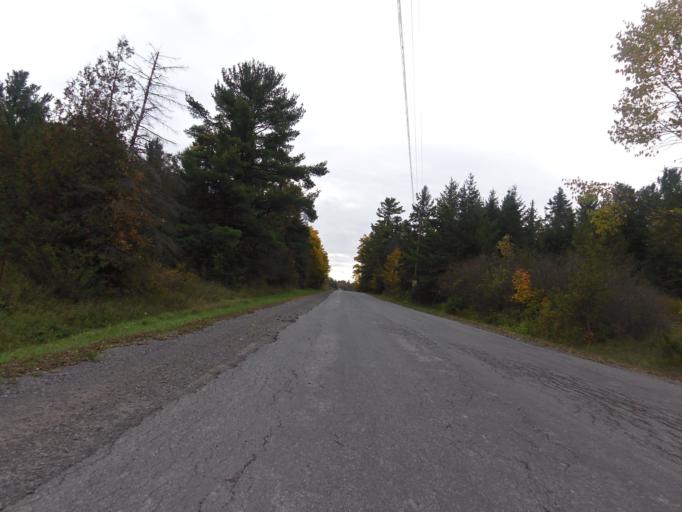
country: CA
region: Ontario
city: Arnprior
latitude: 45.4590
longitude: -76.1420
